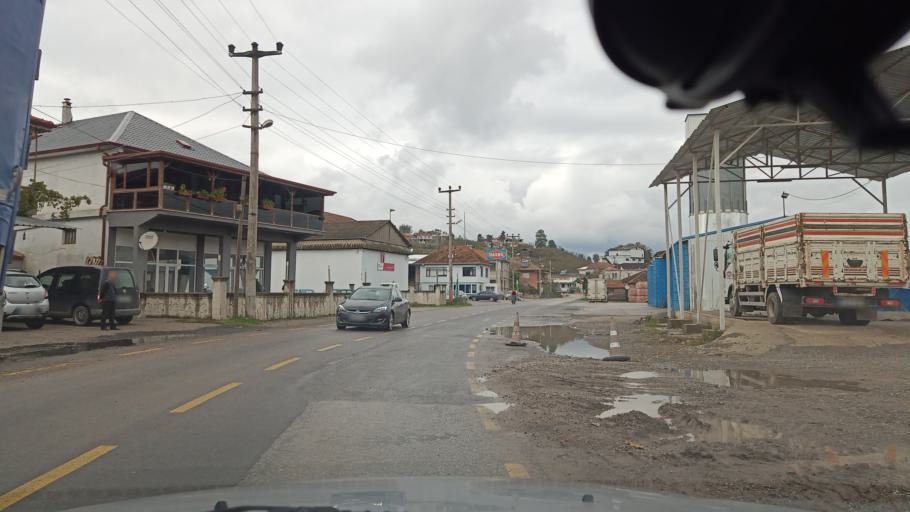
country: TR
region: Sakarya
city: Ortakoy
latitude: 41.0278
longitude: 30.5957
